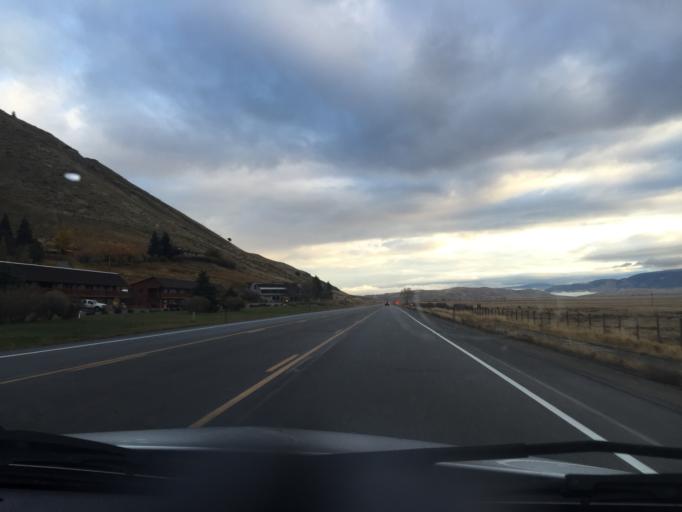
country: US
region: Wyoming
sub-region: Teton County
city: Jackson
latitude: 43.5063
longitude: -110.7568
